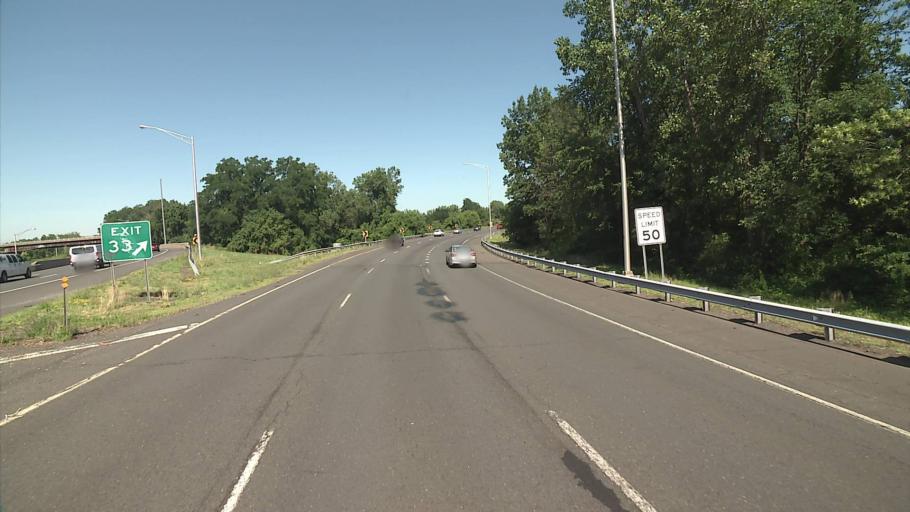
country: US
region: Connecticut
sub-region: Hartford County
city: Plainville
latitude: 41.6706
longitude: -72.8414
